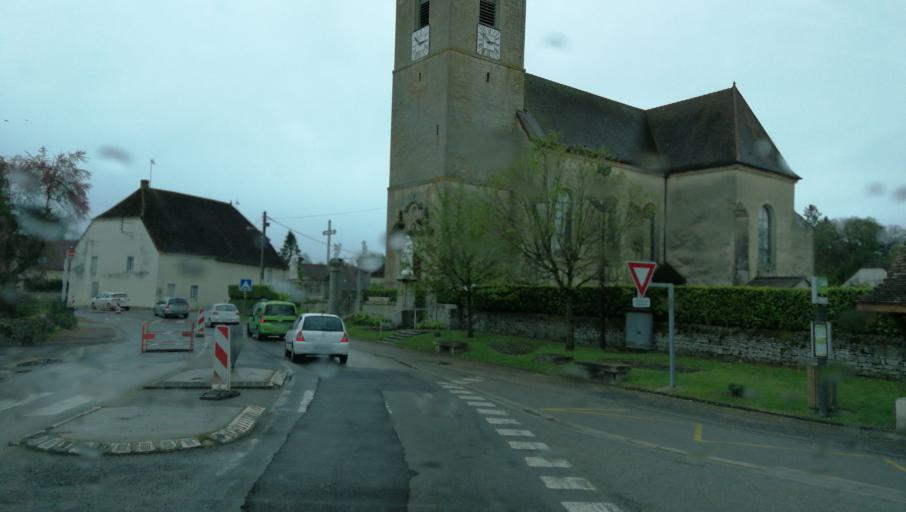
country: FR
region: Franche-Comte
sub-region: Departement du Jura
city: Bletterans
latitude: 46.7369
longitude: 5.4641
